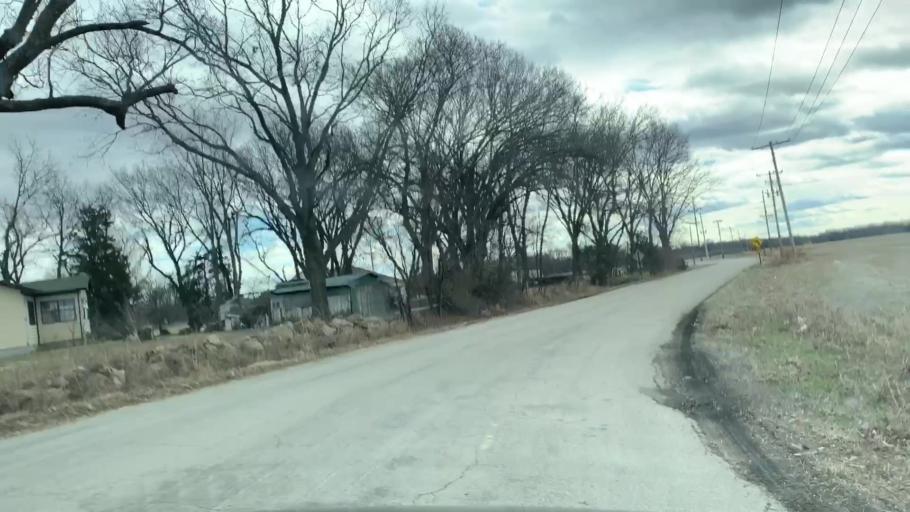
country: US
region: Kansas
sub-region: Allen County
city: Humboldt
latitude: 37.8126
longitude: -95.4525
